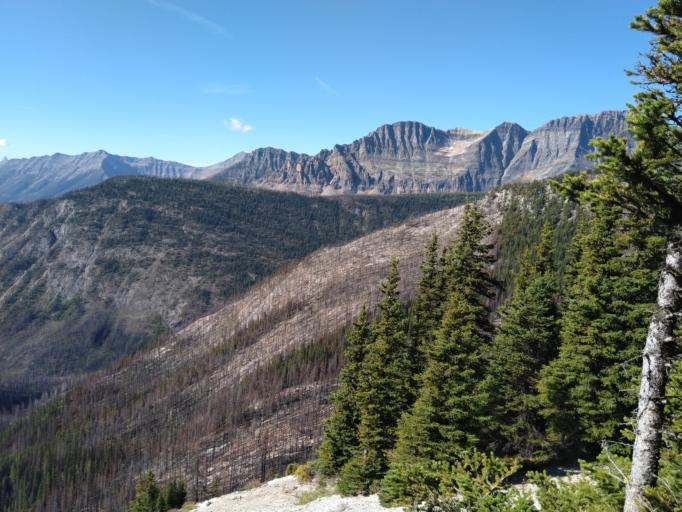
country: CA
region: Alberta
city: Banff
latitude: 51.0536
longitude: -115.7900
